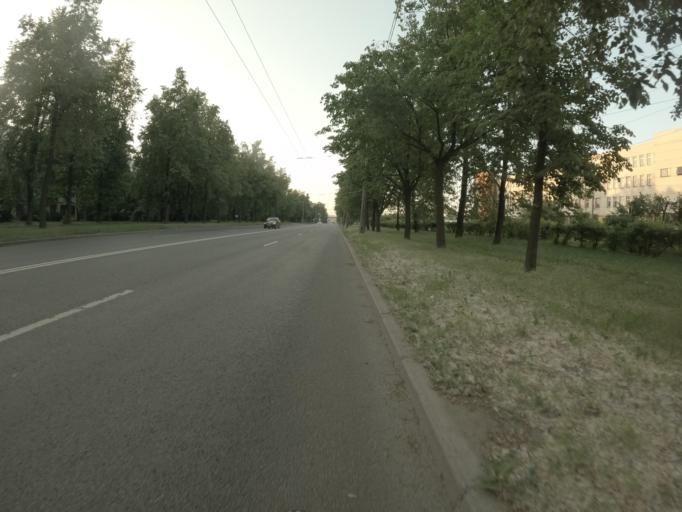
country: RU
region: St.-Petersburg
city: Avtovo
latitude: 59.8745
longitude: 30.2759
